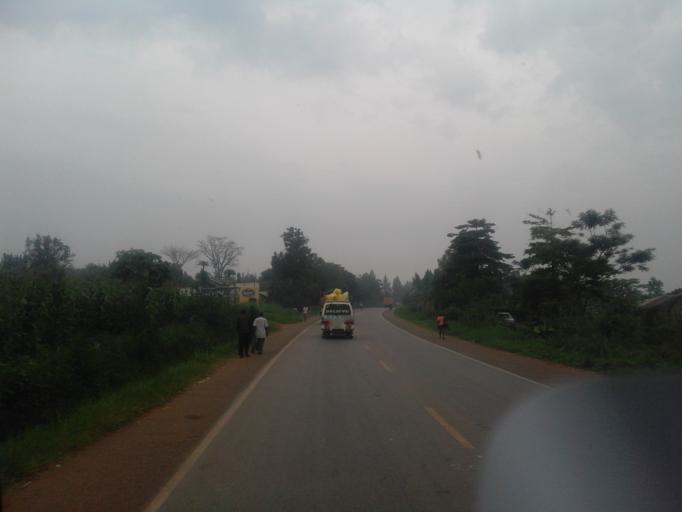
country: UG
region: Central Region
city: Lugazi
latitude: 0.3741
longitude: 32.9159
